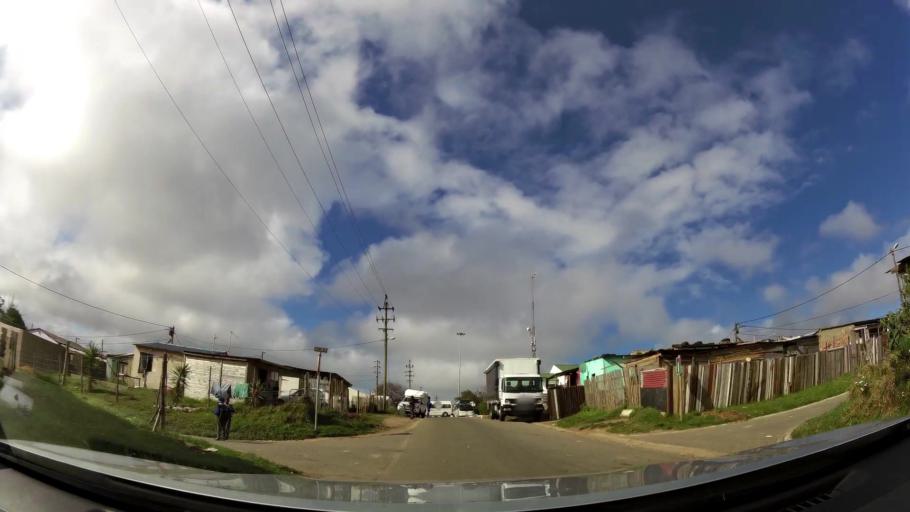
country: ZA
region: Western Cape
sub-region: Eden District Municipality
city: Plettenberg Bay
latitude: -34.0478
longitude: 23.3224
